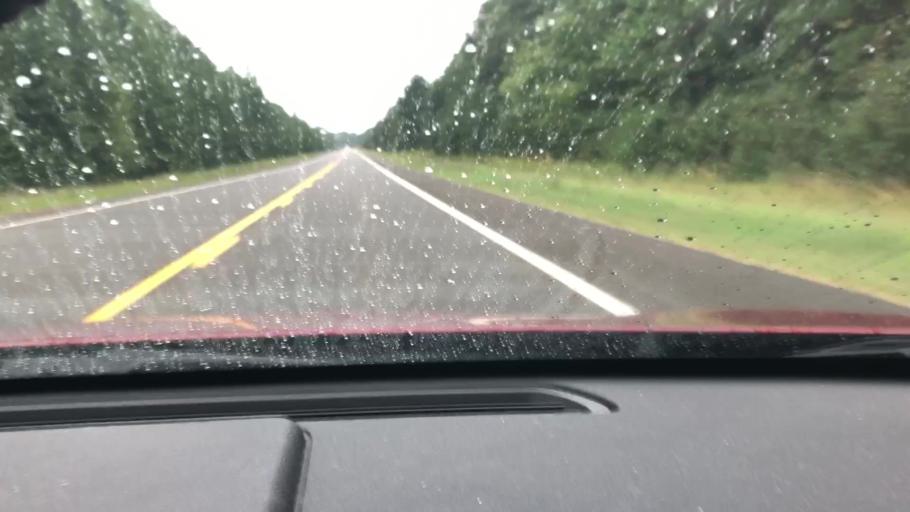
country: US
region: Arkansas
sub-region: Columbia County
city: Waldo
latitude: 33.3062
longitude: -93.2747
